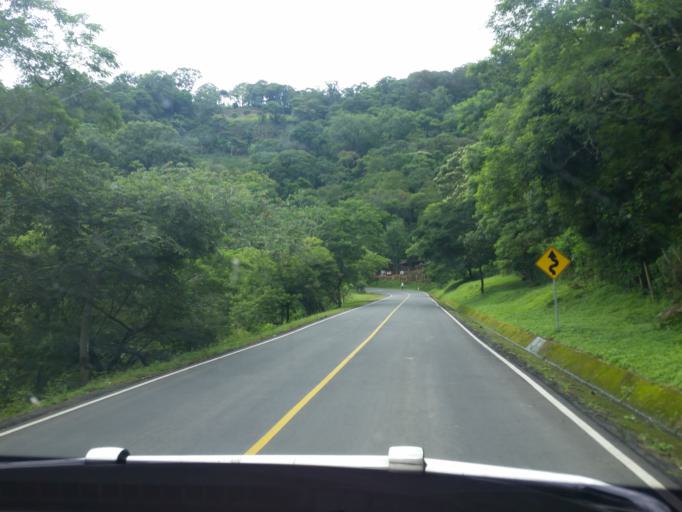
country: NI
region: Jinotega
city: Jinotega
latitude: 13.1363
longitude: -85.9688
